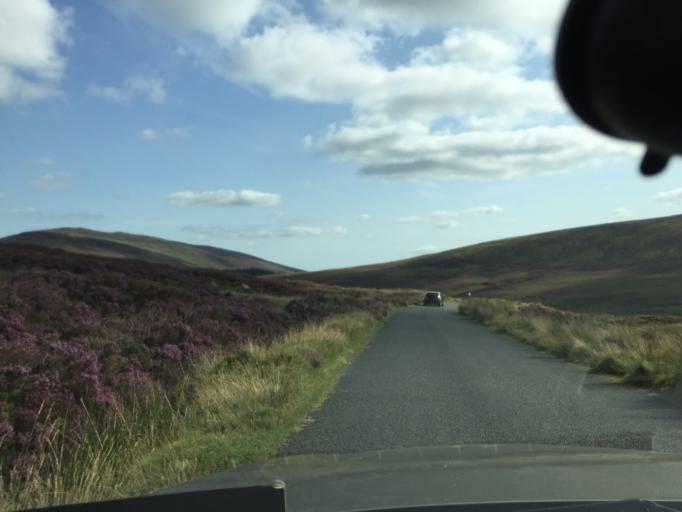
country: IE
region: Leinster
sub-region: Wicklow
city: Rathdrum
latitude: 53.0740
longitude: -6.3527
